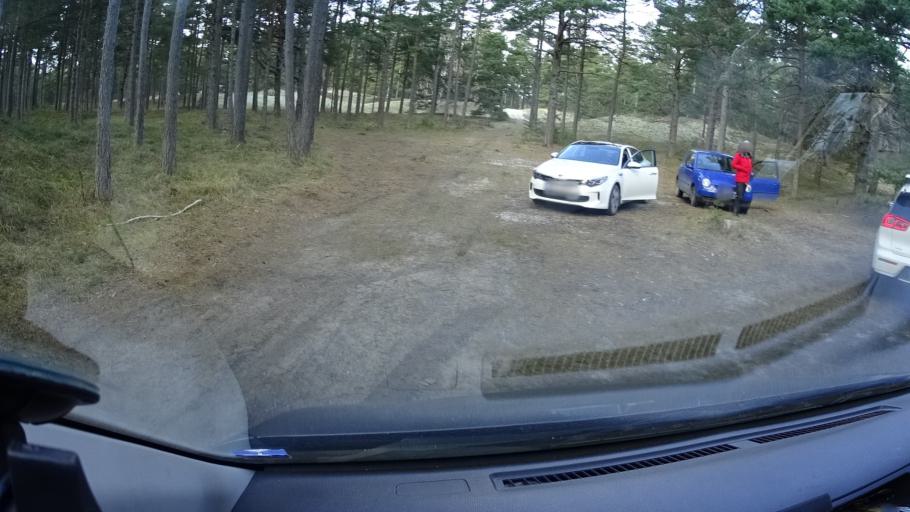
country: SE
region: Gotland
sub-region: Gotland
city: Slite
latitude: 57.9570
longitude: 19.2722
